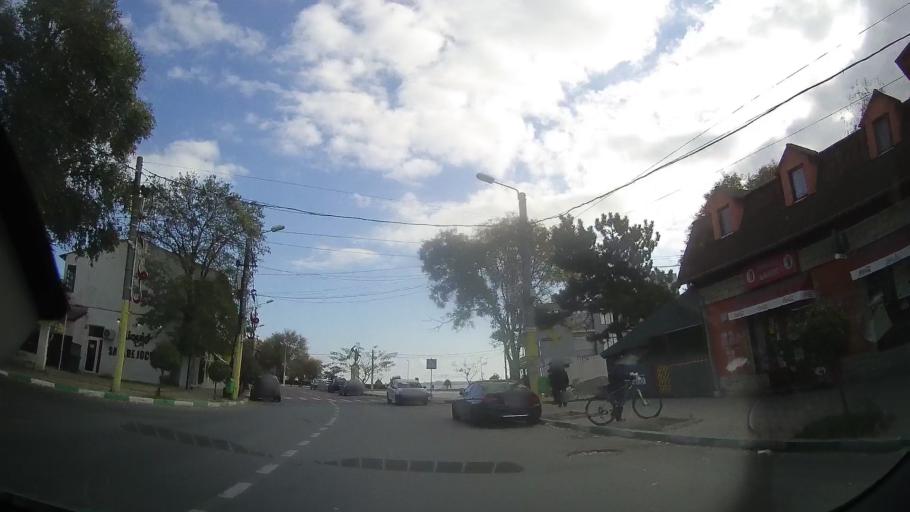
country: RO
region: Constanta
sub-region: Oras Techirghiol
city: Techirghiol
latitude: 44.0551
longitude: 28.6021
